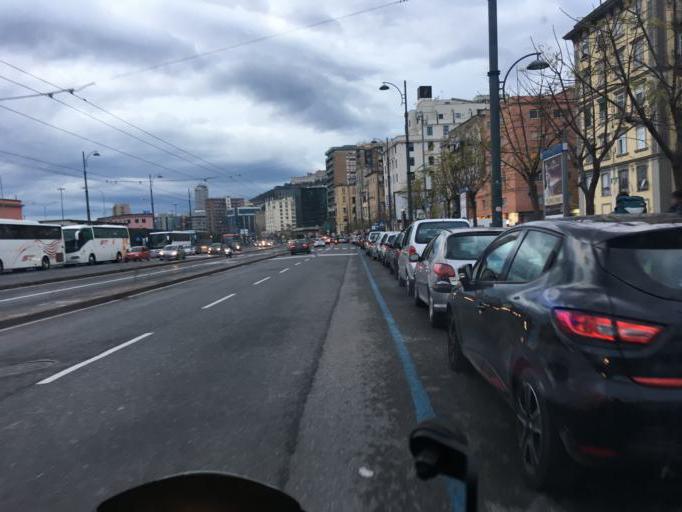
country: IT
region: Campania
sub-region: Provincia di Napoli
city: Napoli
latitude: 40.8462
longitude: 14.2659
